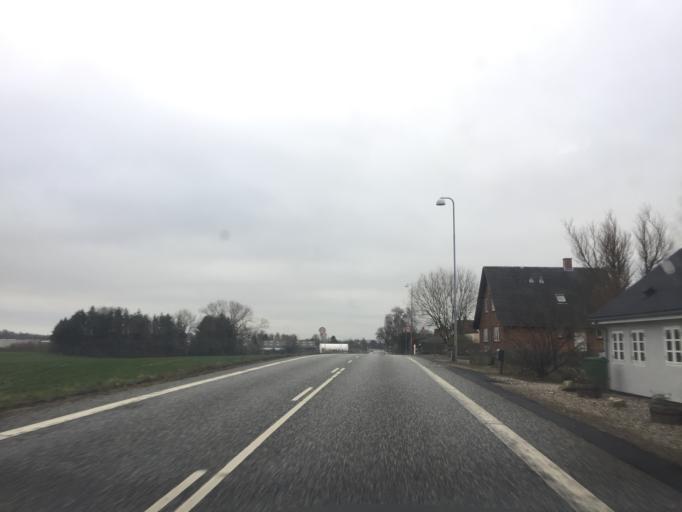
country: DK
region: South Denmark
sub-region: Svendborg Kommune
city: Svendborg
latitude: 55.0919
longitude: 10.6301
